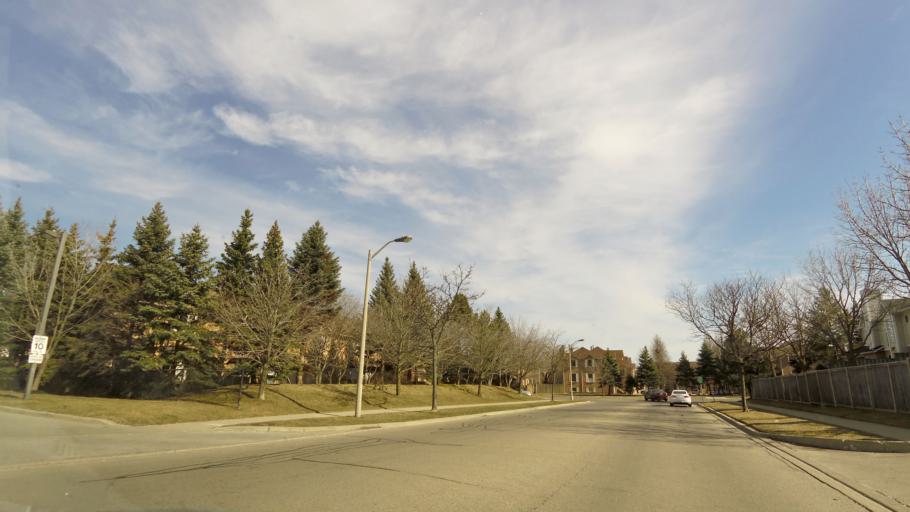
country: CA
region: Ontario
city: Burlington
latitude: 43.3886
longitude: -79.8263
